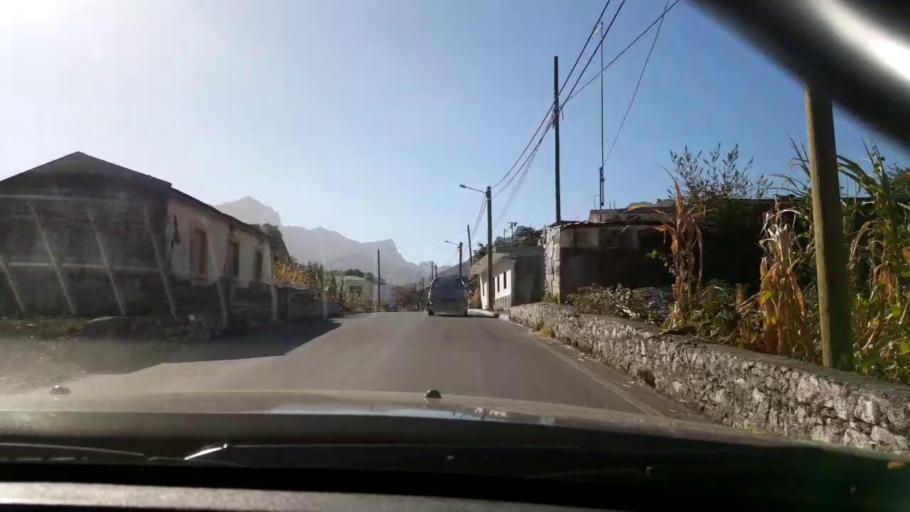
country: CV
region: Sao Lourenco dos Orgaos
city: Joao Teves
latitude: 15.0685
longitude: -23.5782
